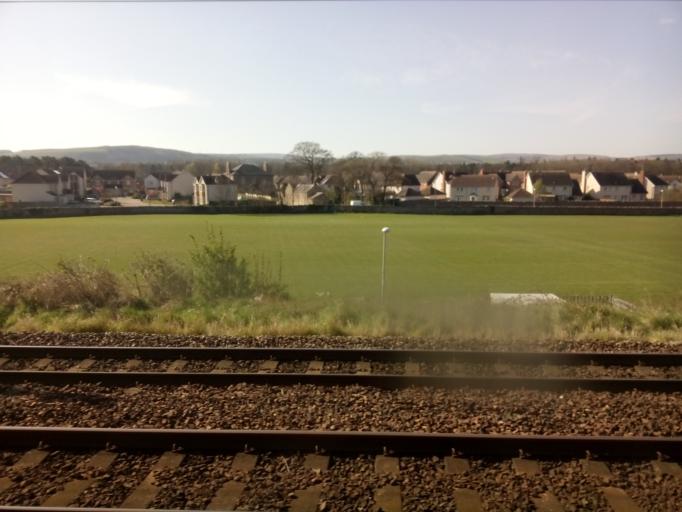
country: GB
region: Scotland
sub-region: East Lothian
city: Dunbar
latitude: 55.9989
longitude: -2.5180
